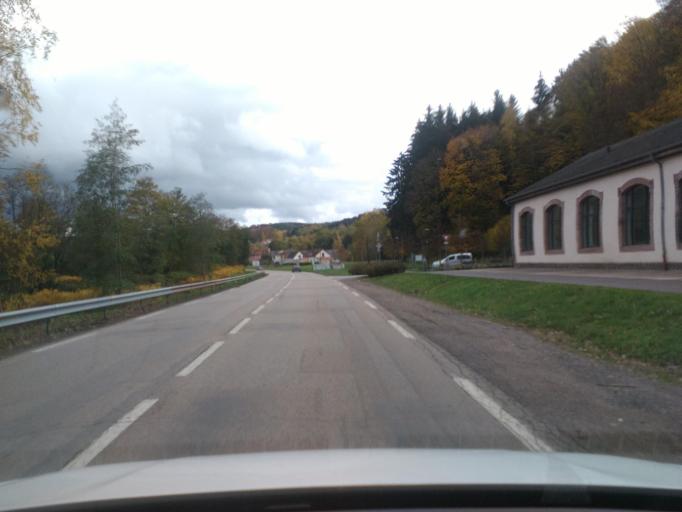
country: FR
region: Lorraine
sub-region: Departement des Vosges
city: Senones
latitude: 48.3913
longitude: 6.9665
